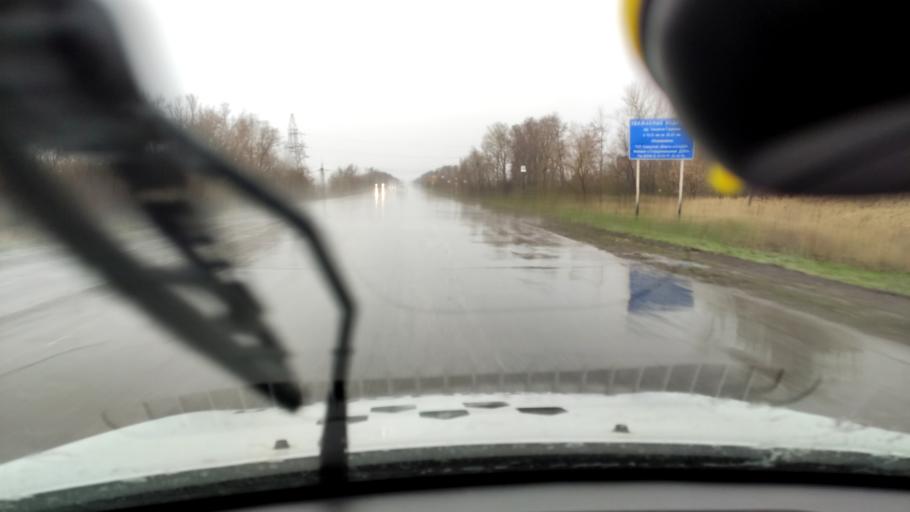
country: RU
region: Samara
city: Tol'yatti
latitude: 53.5834
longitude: 49.4043
